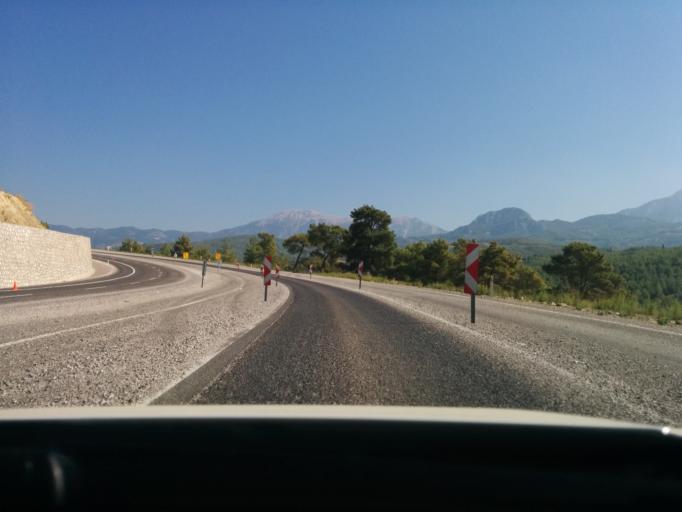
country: TR
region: Mugla
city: Kemer
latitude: 36.6397
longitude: 29.3953
